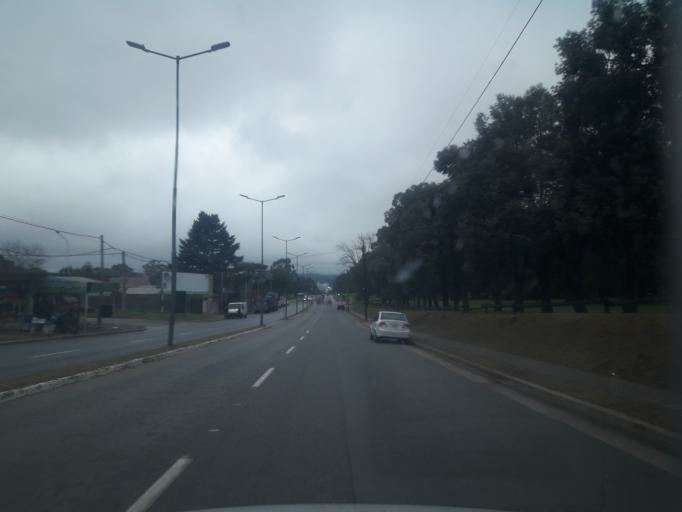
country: AR
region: Buenos Aires
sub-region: Partido de Tandil
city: Tandil
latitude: -37.3037
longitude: -59.1664
